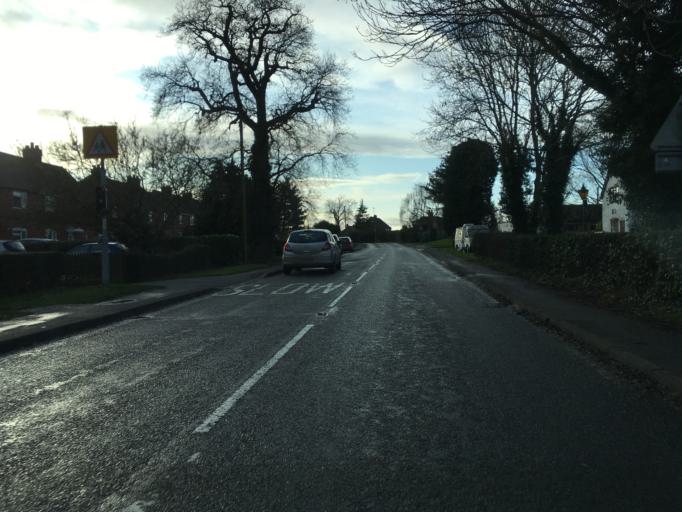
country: GB
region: England
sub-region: Warwickshire
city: Alcester
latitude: 52.2313
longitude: -1.8366
